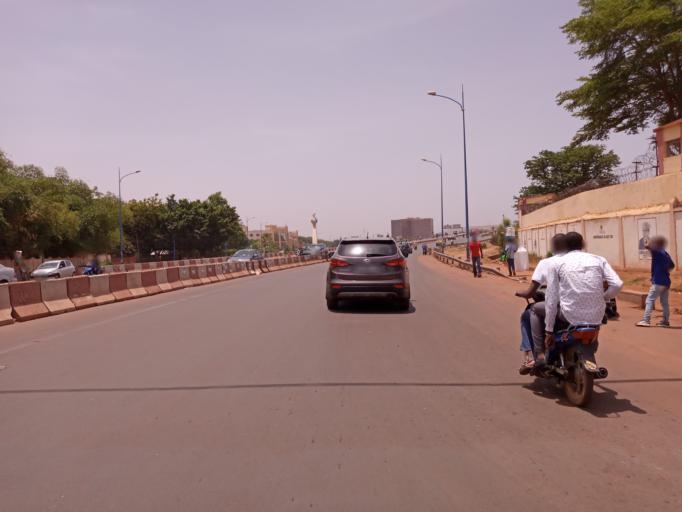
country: ML
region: Bamako
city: Bamako
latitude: 12.6335
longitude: -8.0086
